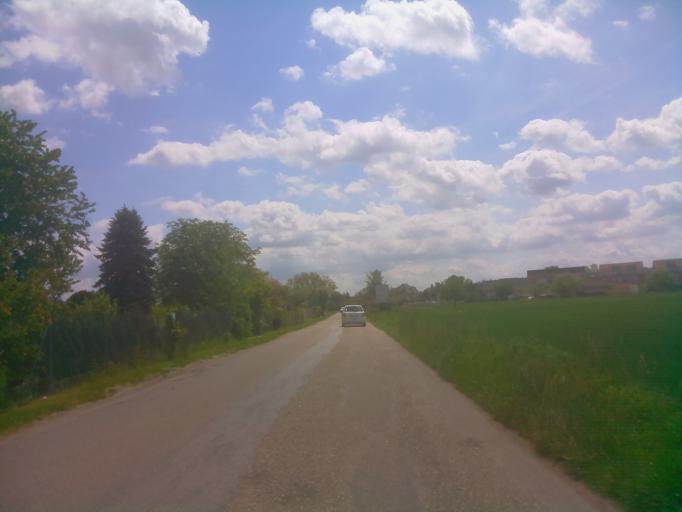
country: DE
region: Rheinland-Pfalz
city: Otterstadt
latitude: 49.3668
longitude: 8.4490
